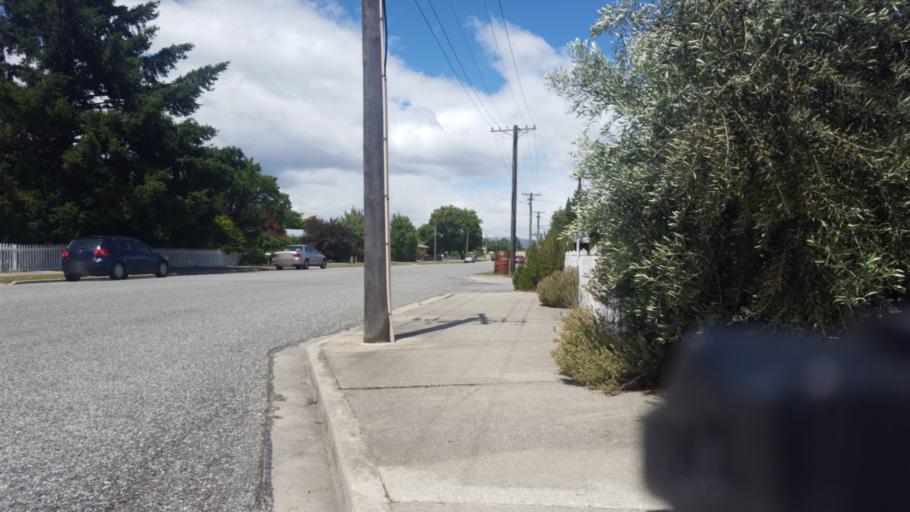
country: NZ
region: Otago
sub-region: Queenstown-Lakes District
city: Wanaka
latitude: -45.1896
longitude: 169.3176
